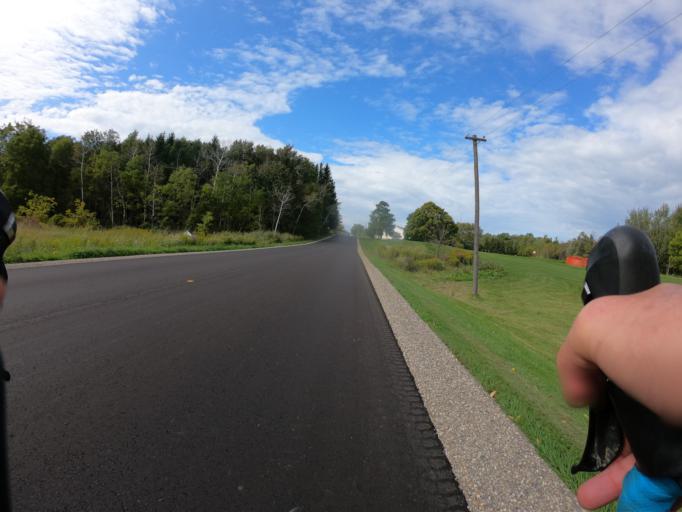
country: CA
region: Ontario
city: Kitchener
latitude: 43.3837
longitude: -80.6253
